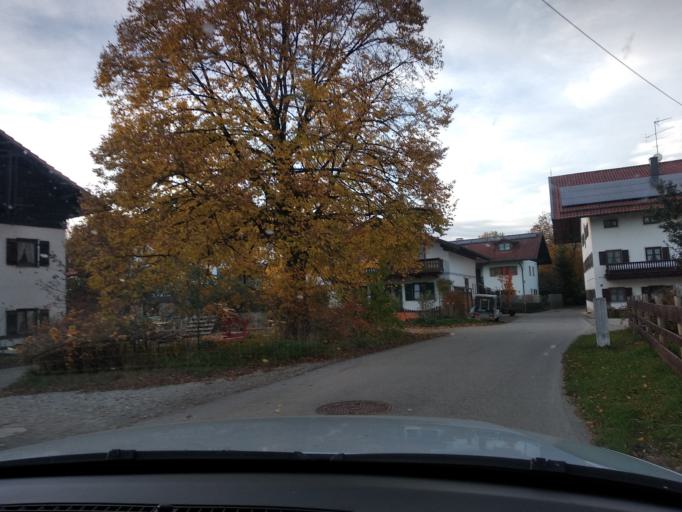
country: DE
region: Bavaria
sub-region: Upper Bavaria
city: Grafing bei Munchen
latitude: 48.0344
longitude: 11.9898
